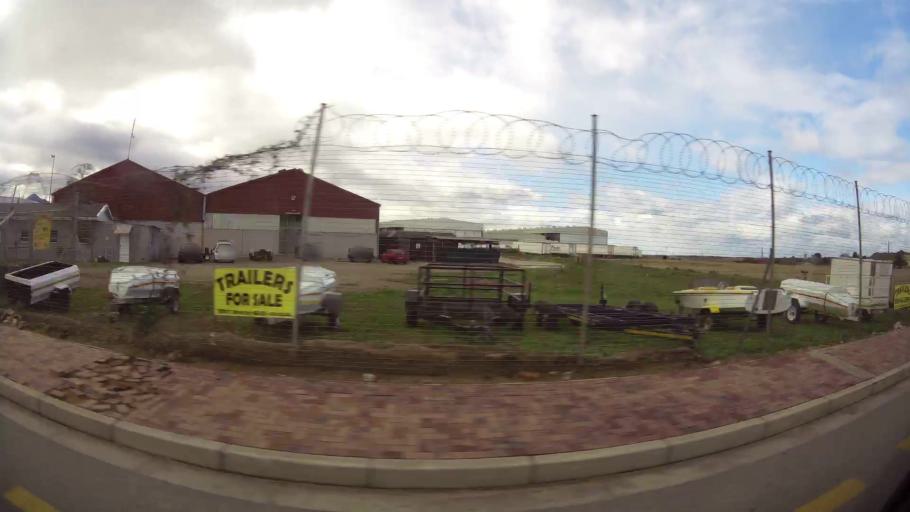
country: ZA
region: Western Cape
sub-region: Eden District Municipality
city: George
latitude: -33.9774
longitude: 22.4716
